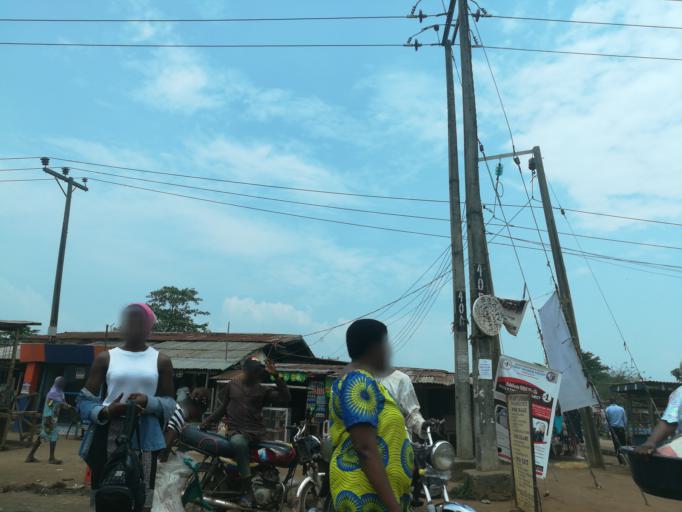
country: NG
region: Lagos
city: Ikorodu
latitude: 6.5810
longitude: 3.5890
